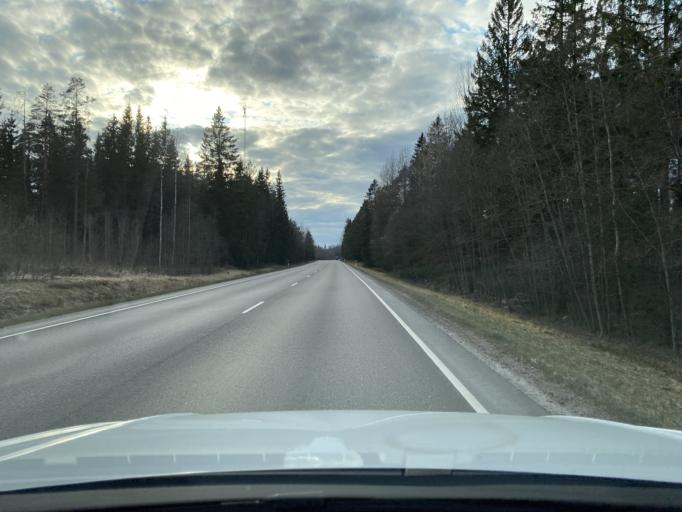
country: FI
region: Haeme
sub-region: Haemeenlinna
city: Renko
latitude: 60.7855
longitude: 24.1439
